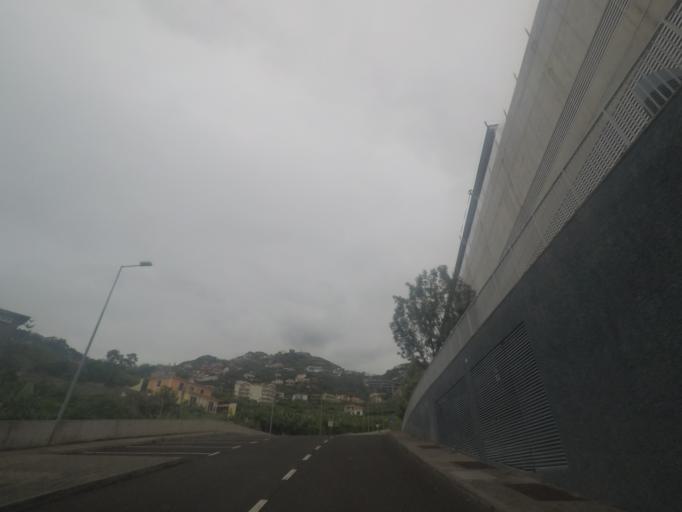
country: PT
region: Madeira
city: Camara de Lobos
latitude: 32.6544
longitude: -16.9827
